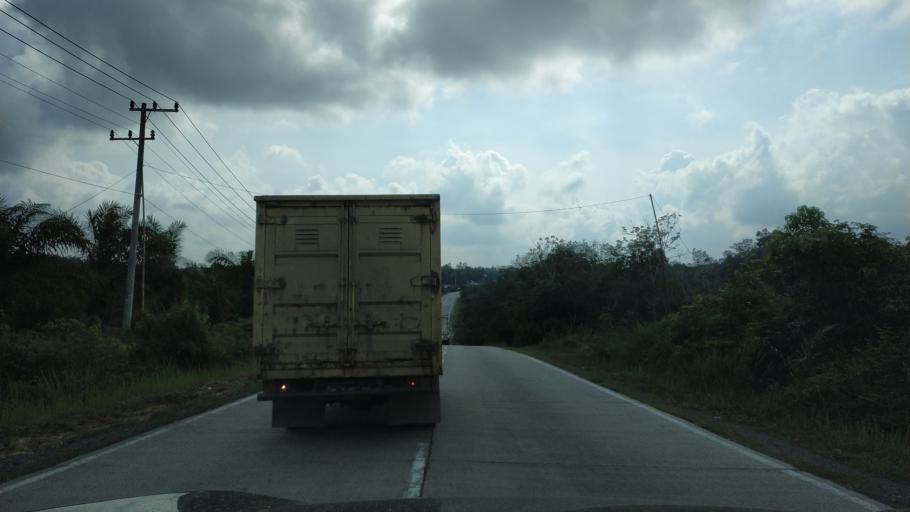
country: ID
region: Riau
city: Pangkalan Kasai
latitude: -0.6964
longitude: 102.4853
